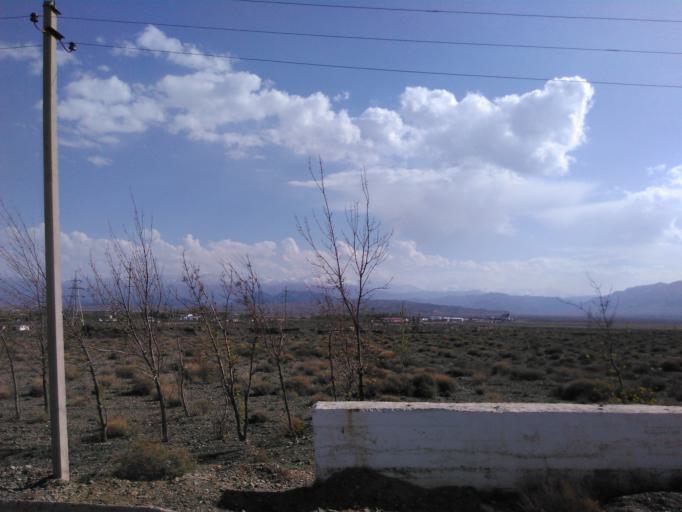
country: KG
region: Ysyk-Koel
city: Balykchy
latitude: 42.4554
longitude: 76.1515
